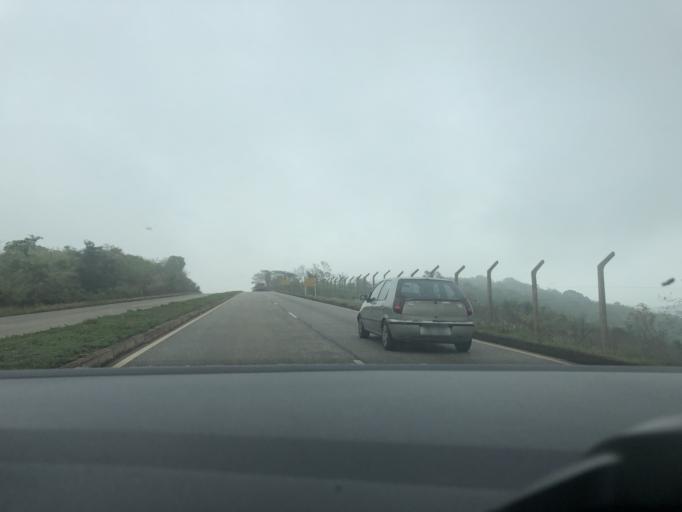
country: BR
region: Minas Gerais
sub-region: Congonhas
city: Congonhas
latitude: -20.5936
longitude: -43.9505
